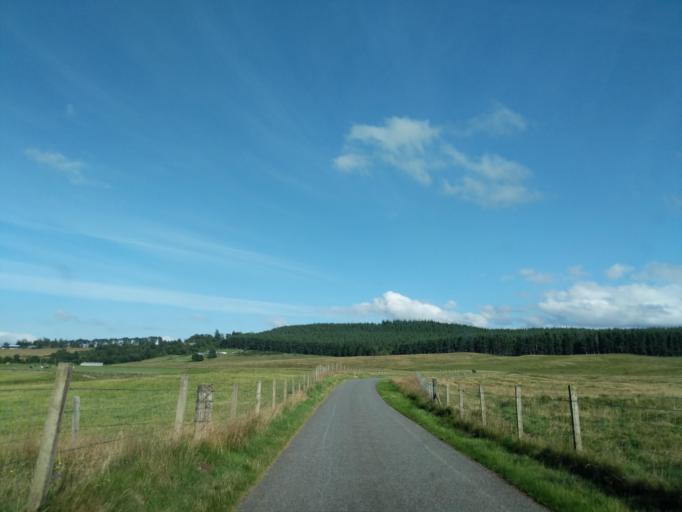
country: GB
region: Scotland
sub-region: Highland
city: Grantown on Spey
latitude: 57.2893
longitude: -3.7316
